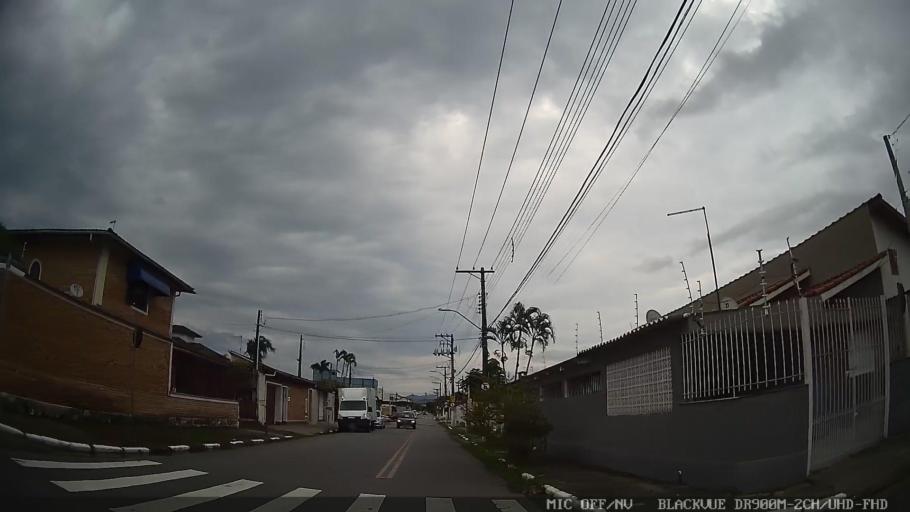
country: BR
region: Sao Paulo
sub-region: Caraguatatuba
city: Caraguatatuba
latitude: -23.6204
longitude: -45.4143
